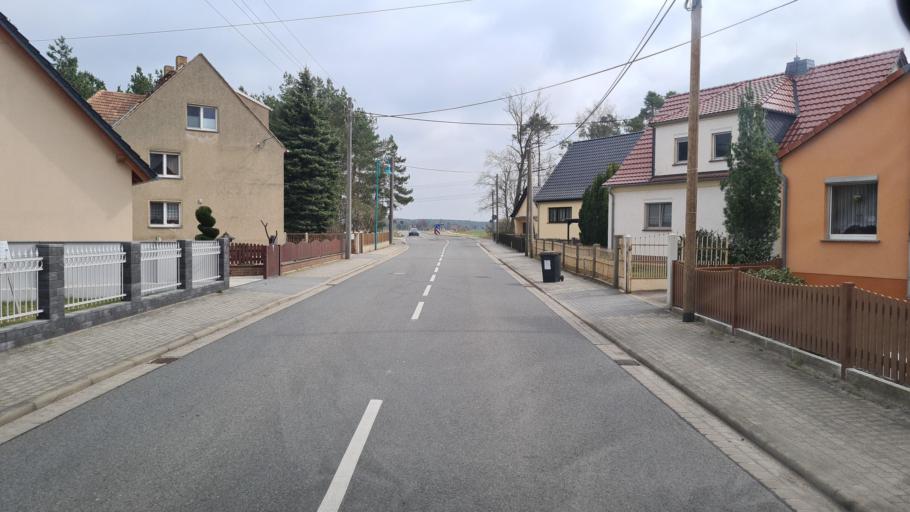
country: DE
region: Saxony
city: Zabeltitz
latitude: 51.3883
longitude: 13.4895
